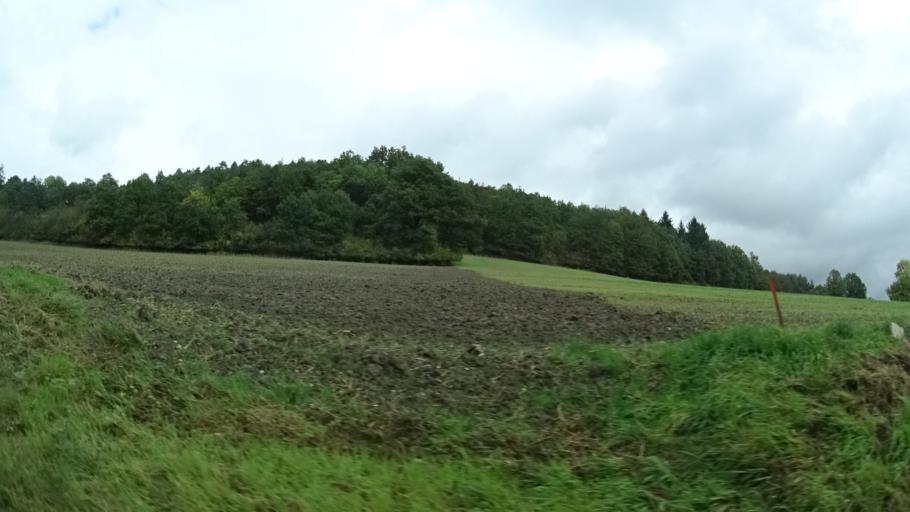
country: DE
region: Bavaria
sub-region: Upper Franconia
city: Priesendorf
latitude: 49.9005
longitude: 10.7166
